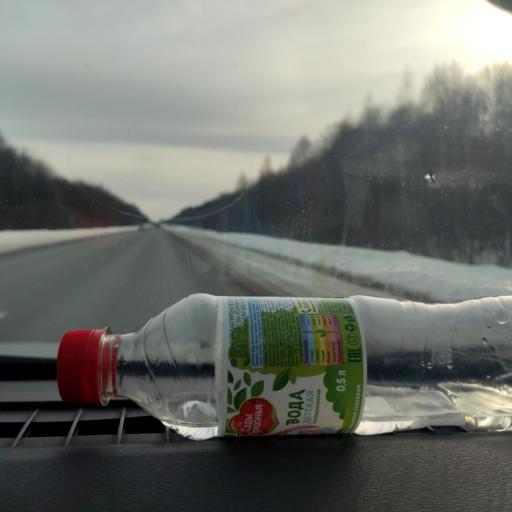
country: RU
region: Bashkortostan
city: Blagoveshchensk
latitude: 54.9808
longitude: 56.0914
